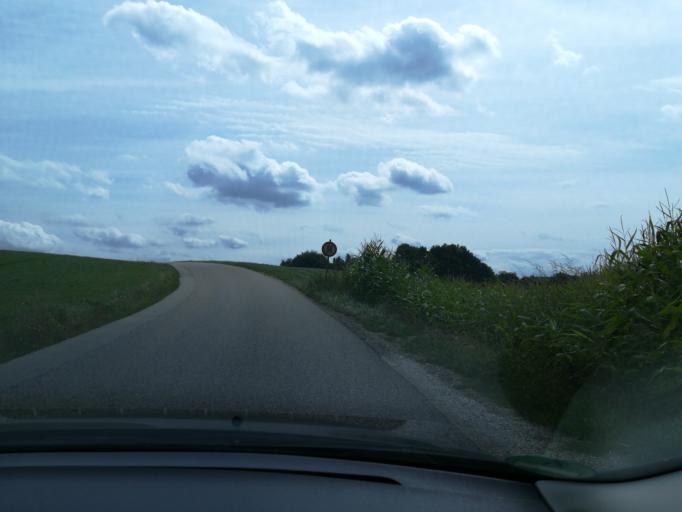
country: DE
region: Bavaria
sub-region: Upper Bavaria
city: Bruck
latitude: 48.0335
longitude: 11.9007
